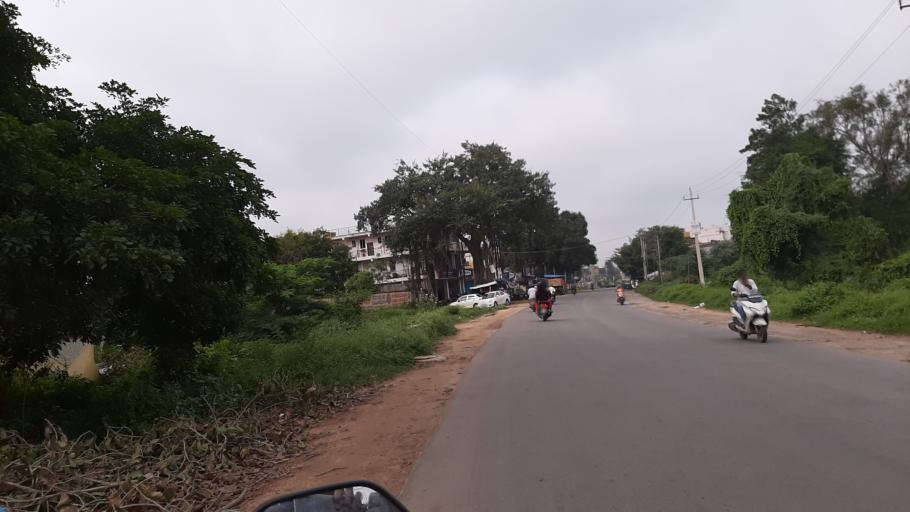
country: IN
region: Karnataka
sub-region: Bangalore Rural
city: Nelamangala
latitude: 12.9679
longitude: 77.4053
